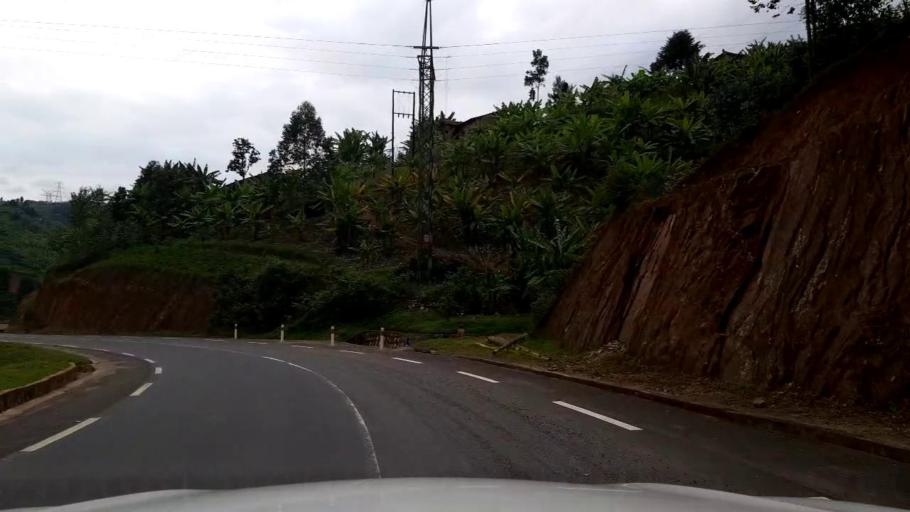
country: RW
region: Western Province
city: Kibuye
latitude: -1.9119
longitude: 29.3687
